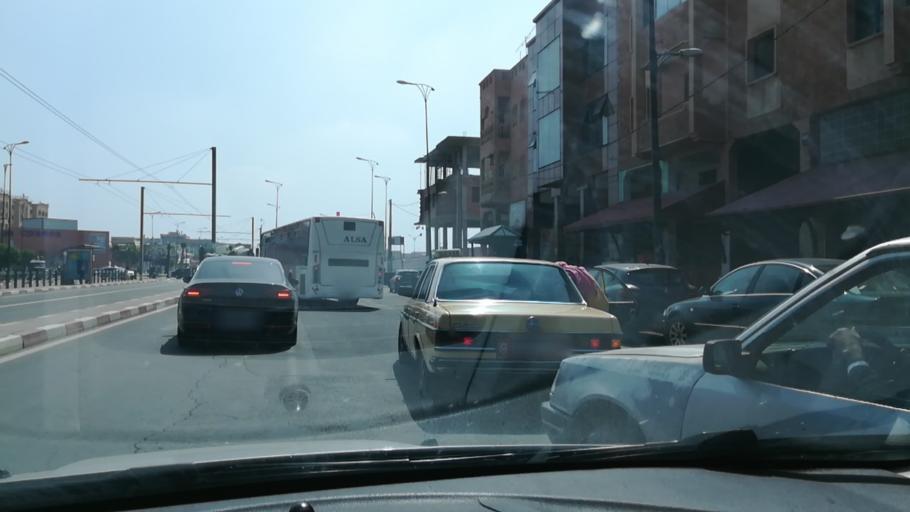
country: MA
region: Marrakech-Tensift-Al Haouz
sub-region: Marrakech
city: Marrakesh
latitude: 31.6277
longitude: -8.0598
